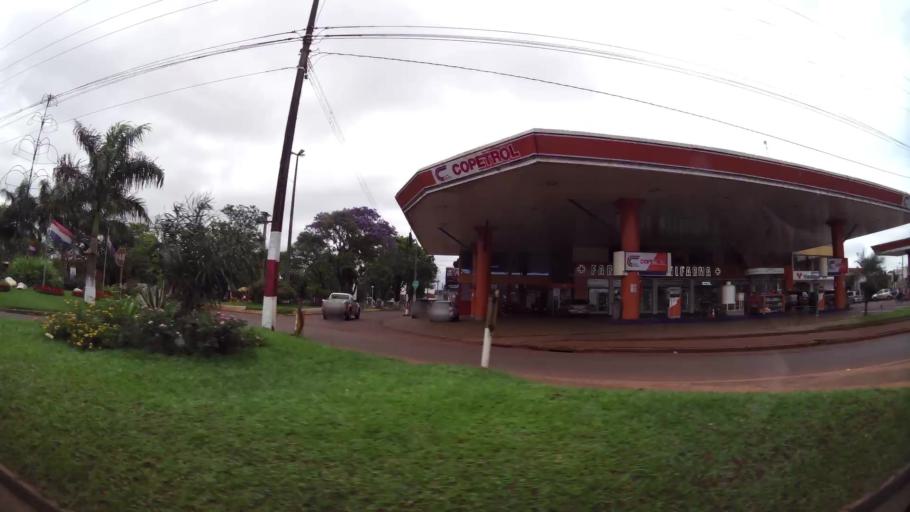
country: PY
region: Alto Parana
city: Ciudad del Este
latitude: -25.4081
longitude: -54.6302
